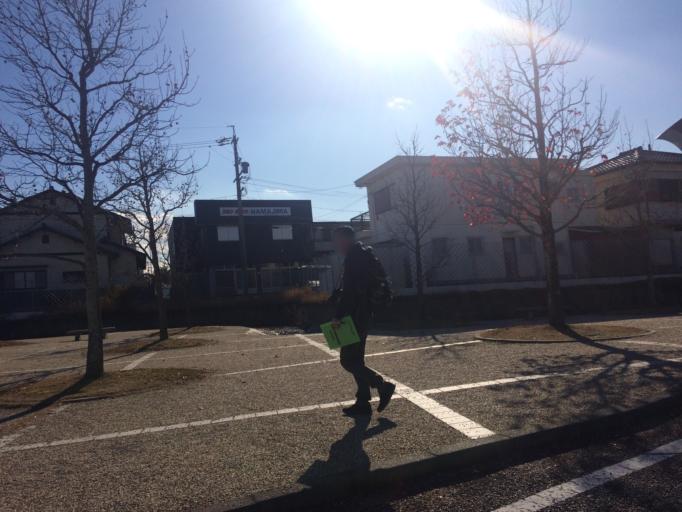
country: JP
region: Aichi
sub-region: Toyota-shi
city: Toyota
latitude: 35.1298
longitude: 137.0401
